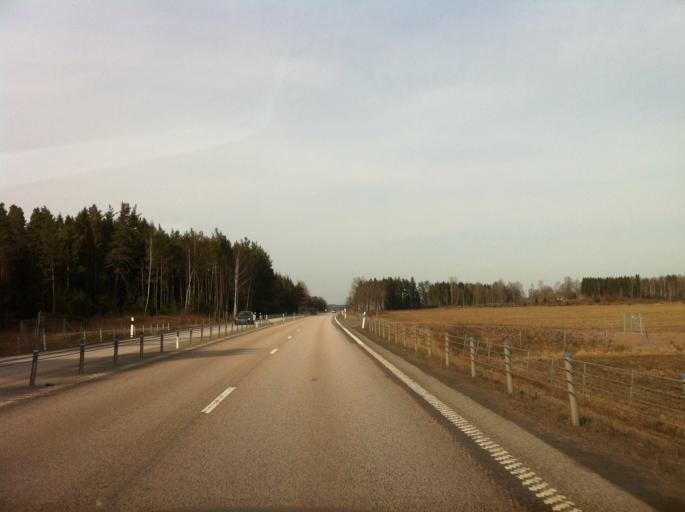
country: SE
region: Vaestra Goetaland
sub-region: Skovde Kommun
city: Stopen
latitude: 58.5383
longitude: 13.8129
